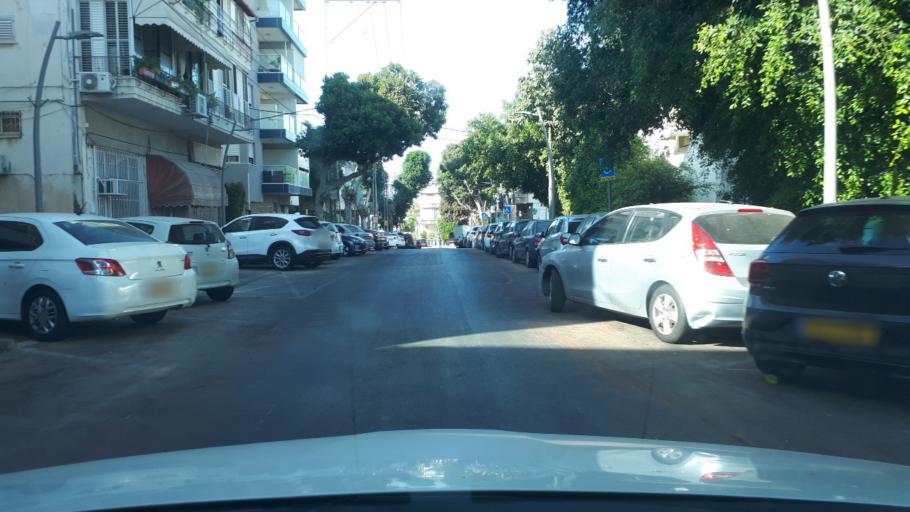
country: IL
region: Tel Aviv
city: Bene Beraq
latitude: 32.0780
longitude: 34.8233
